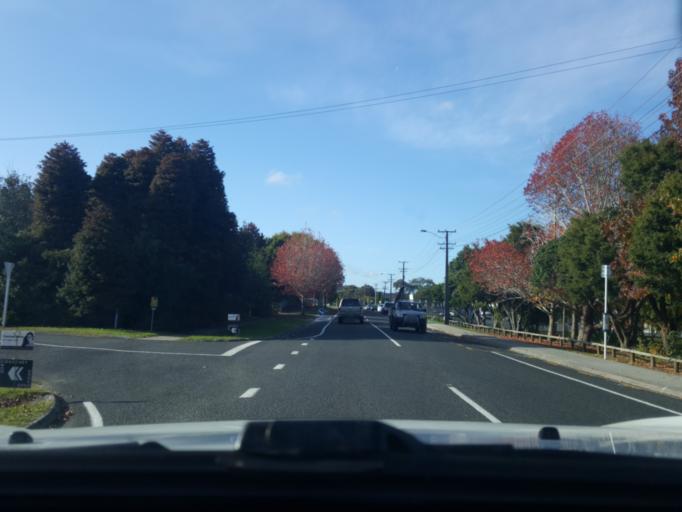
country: NZ
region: Auckland
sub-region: Auckland
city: Rosebank
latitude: -36.7602
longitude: 174.5896
